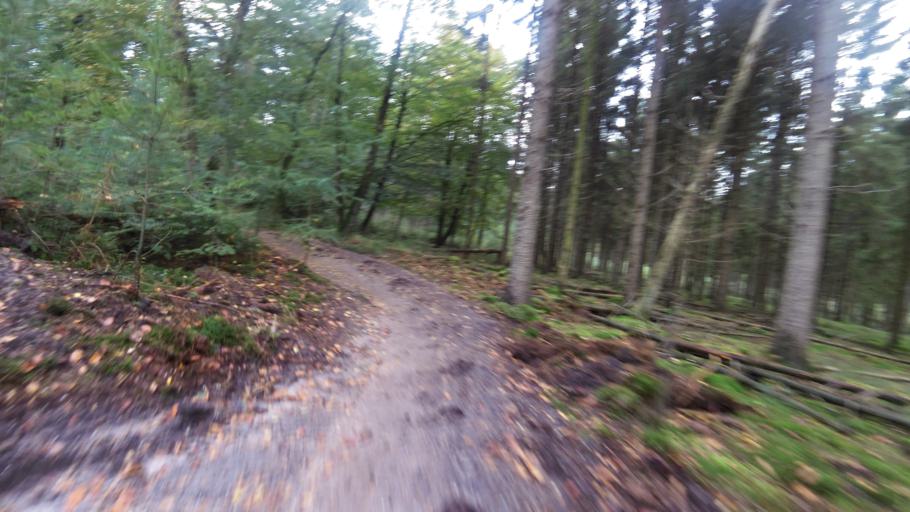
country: NL
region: Gelderland
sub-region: Gemeente Ede
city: Wekerom
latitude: 52.0786
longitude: 5.7336
